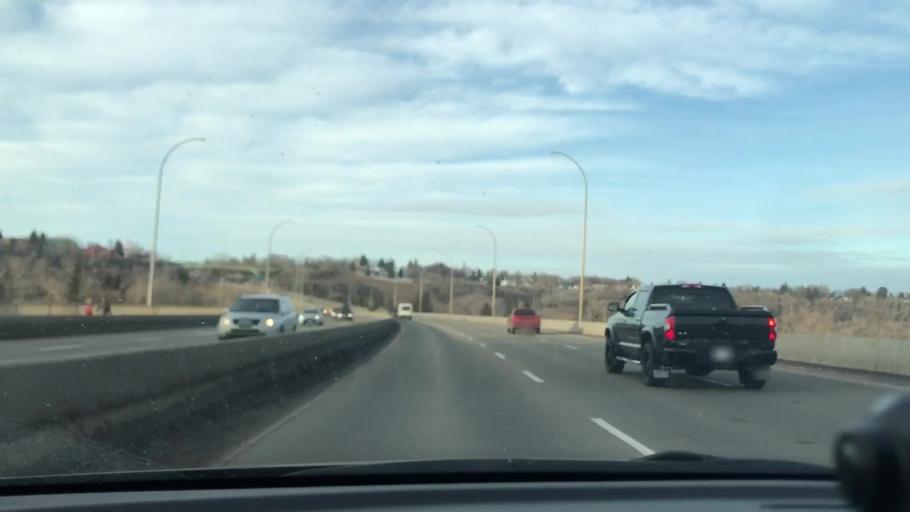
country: CA
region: Alberta
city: Edmonton
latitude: 53.5546
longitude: -113.4381
